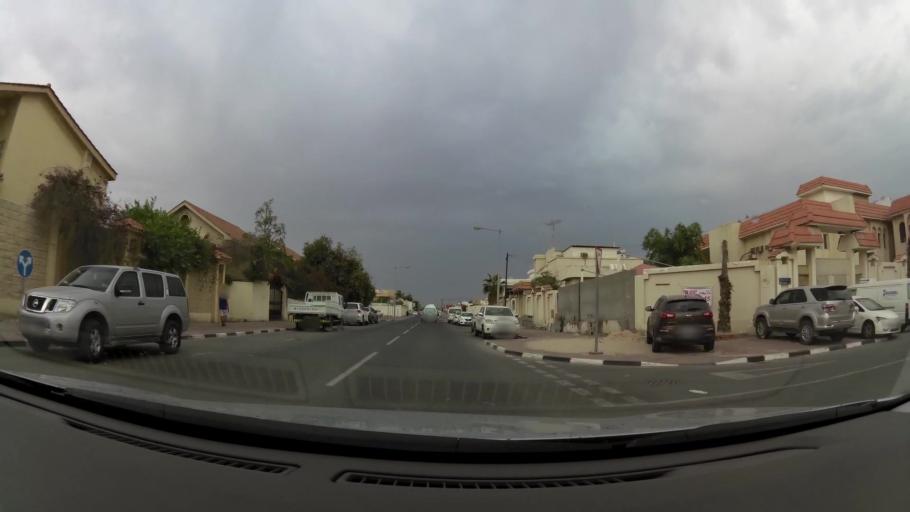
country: QA
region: Baladiyat ad Dawhah
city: Doha
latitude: 25.2679
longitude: 51.4970
